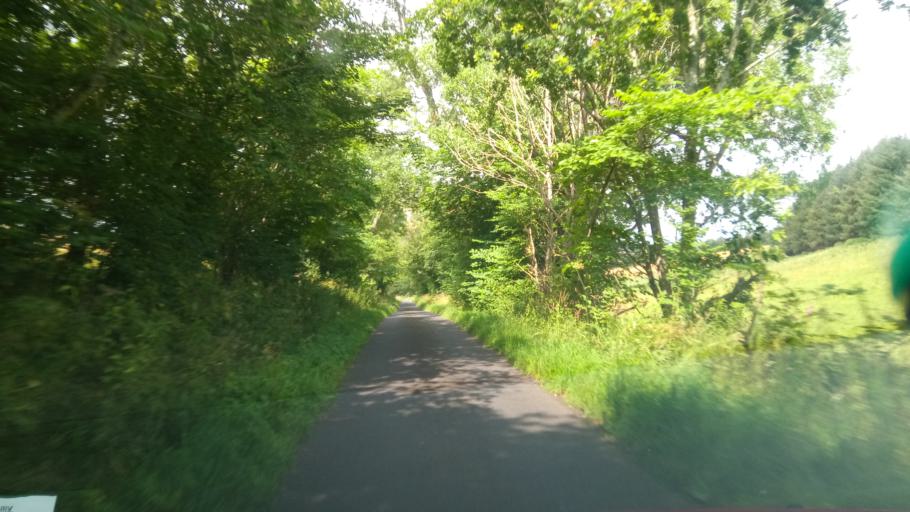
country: GB
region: Scotland
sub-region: The Scottish Borders
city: Jedburgh
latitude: 55.4640
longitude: -2.6391
